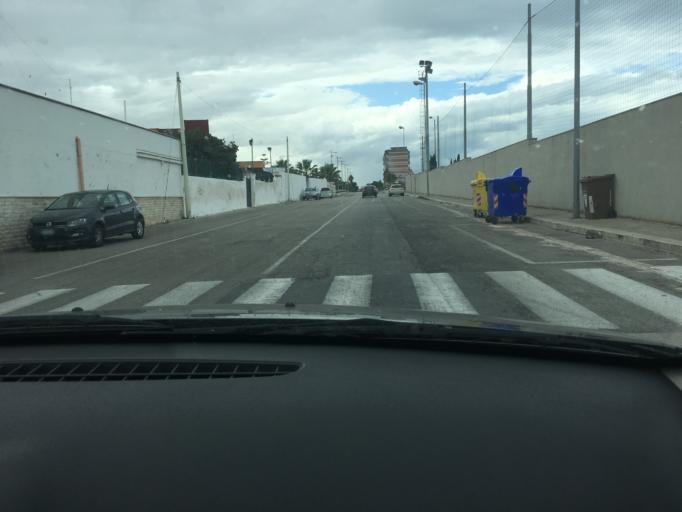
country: IT
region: Apulia
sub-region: Provincia di Bari
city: Bari
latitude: 41.1328
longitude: 16.8302
